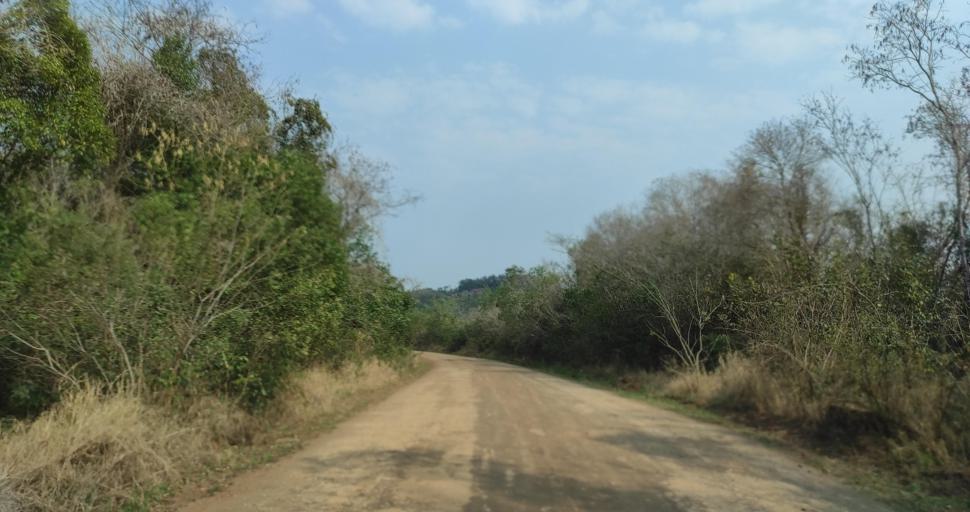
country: AR
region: Misiones
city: Cerro Cora
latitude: -27.5933
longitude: -55.5784
